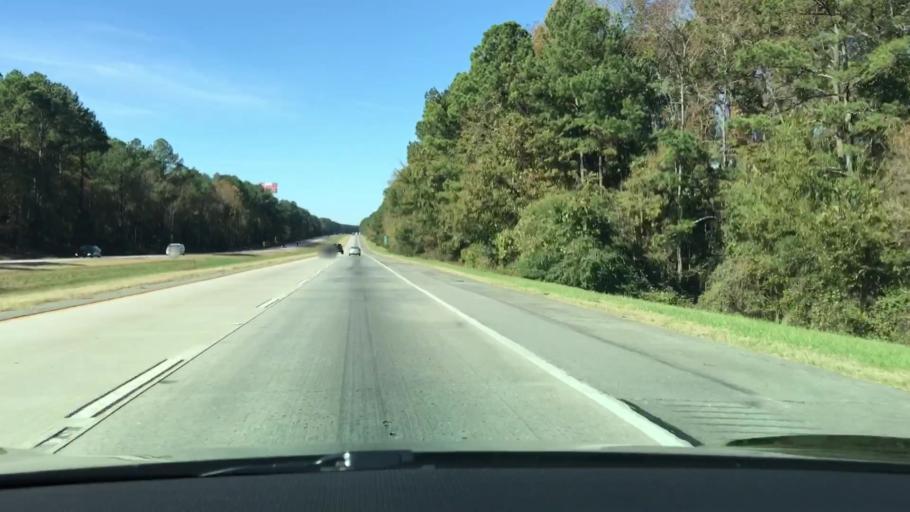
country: US
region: Georgia
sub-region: Taliaferro County
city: Crawfordville
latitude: 33.5289
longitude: -82.9637
